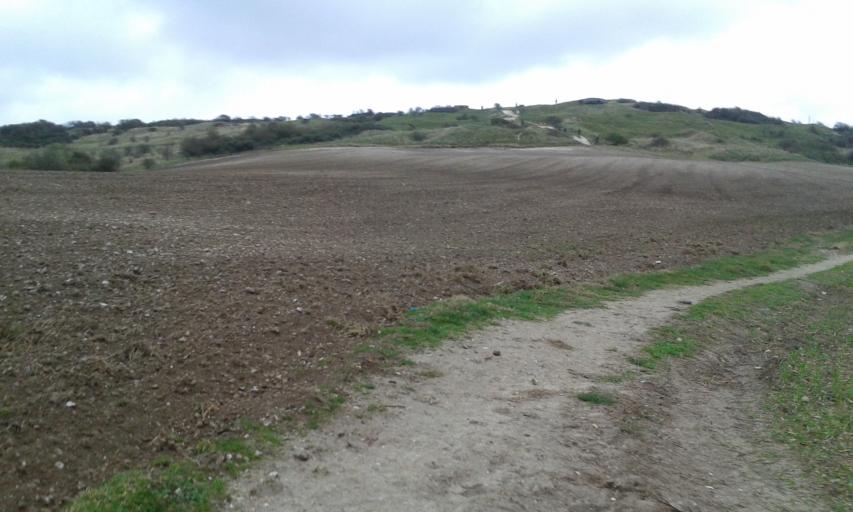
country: FR
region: Nord-Pas-de-Calais
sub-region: Departement du Pas-de-Calais
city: Wissant
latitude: 50.8726
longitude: 1.7017
